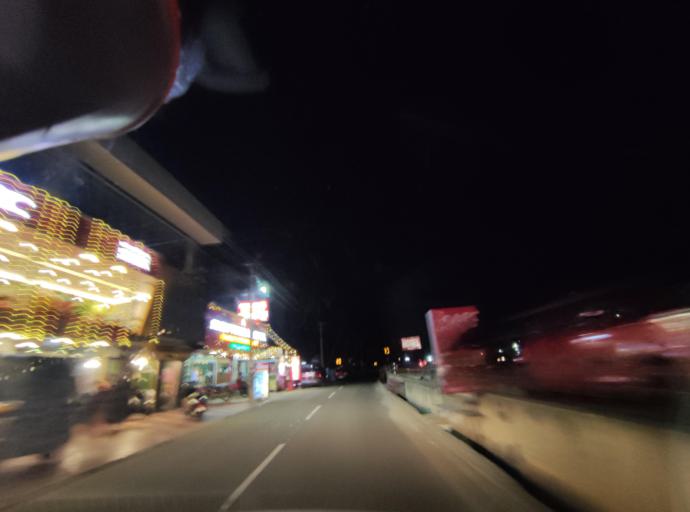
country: IN
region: Kerala
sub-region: Thiruvananthapuram
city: Thiruvananthapuram
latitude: 8.4787
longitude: 76.9353
